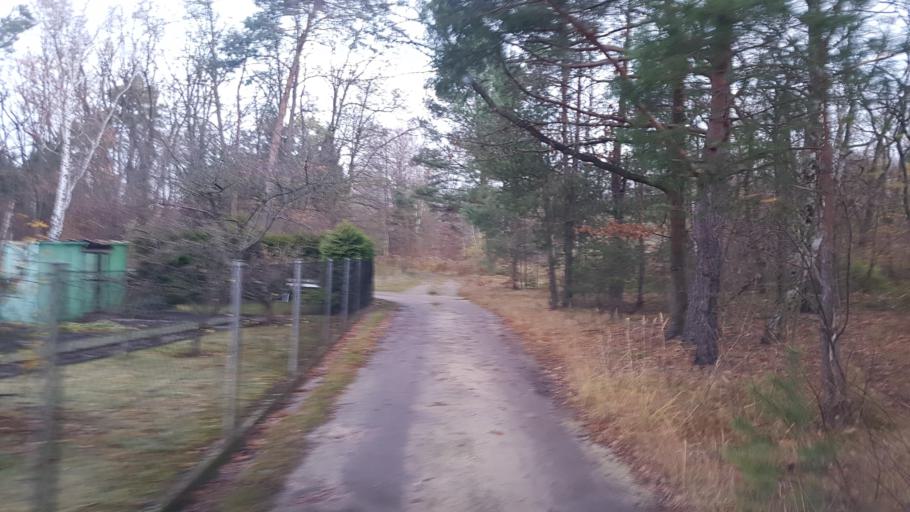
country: DE
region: Brandenburg
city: Lauchhammer
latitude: 51.5093
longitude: 13.7599
